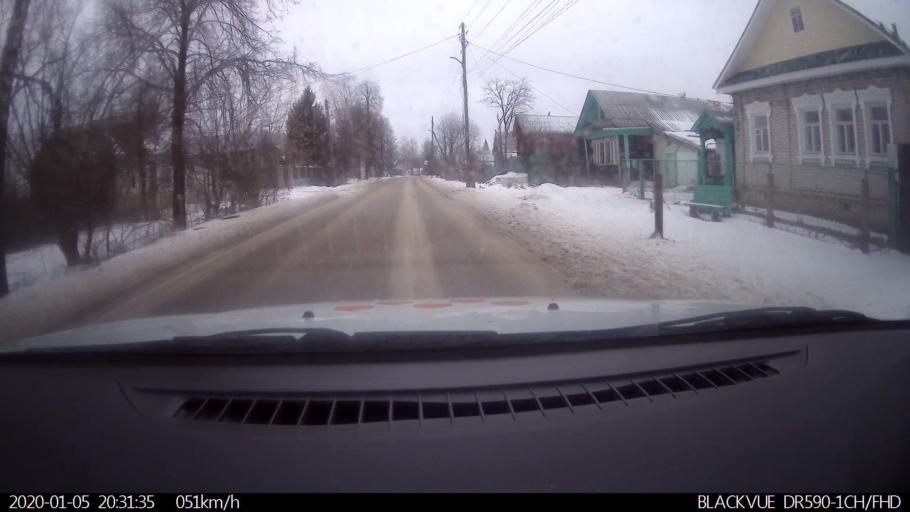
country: RU
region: Nizjnij Novgorod
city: Lukino
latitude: 56.4071
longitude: 43.7286
